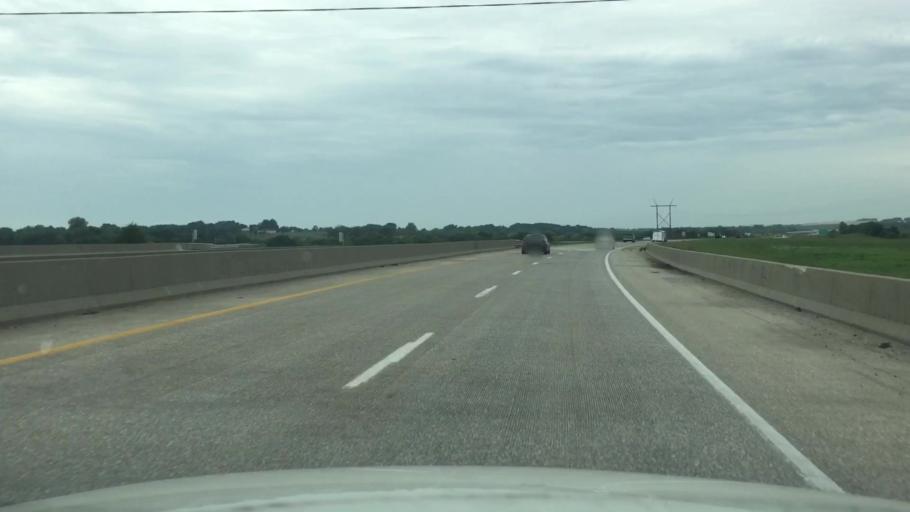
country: US
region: Iowa
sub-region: Warren County
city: Norwalk
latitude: 41.4989
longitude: -93.6254
